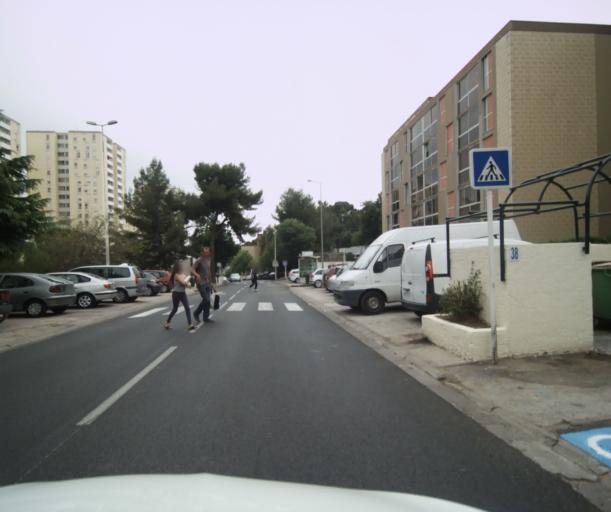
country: FR
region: Provence-Alpes-Cote d'Azur
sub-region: Departement du Var
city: Ollioules
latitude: 43.1336
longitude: 5.8819
